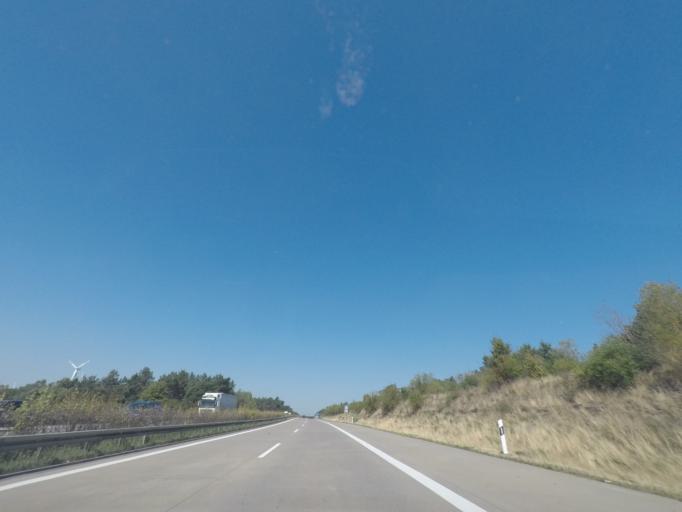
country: DE
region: Brandenburg
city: Luebben
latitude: 51.9030
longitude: 13.8084
